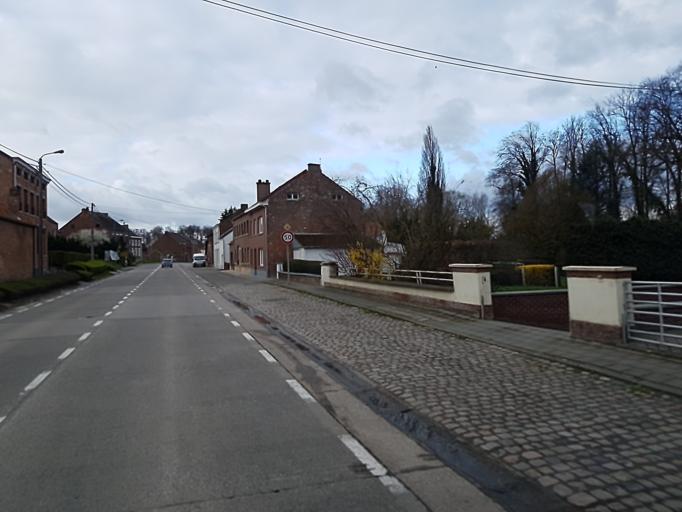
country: BE
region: Flanders
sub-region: Provincie Vlaams-Brabant
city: Hoegaarden
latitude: 50.7634
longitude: 4.9029
